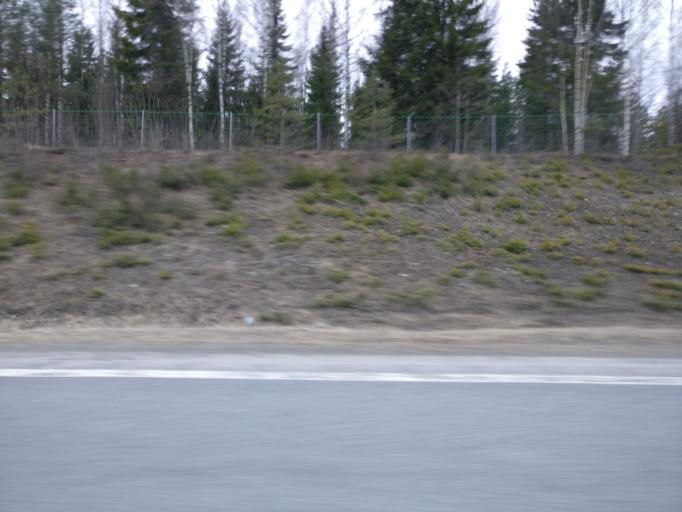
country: FI
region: Pirkanmaa
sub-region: Tampere
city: Lempaeaelae
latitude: 61.3613
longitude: 23.7916
